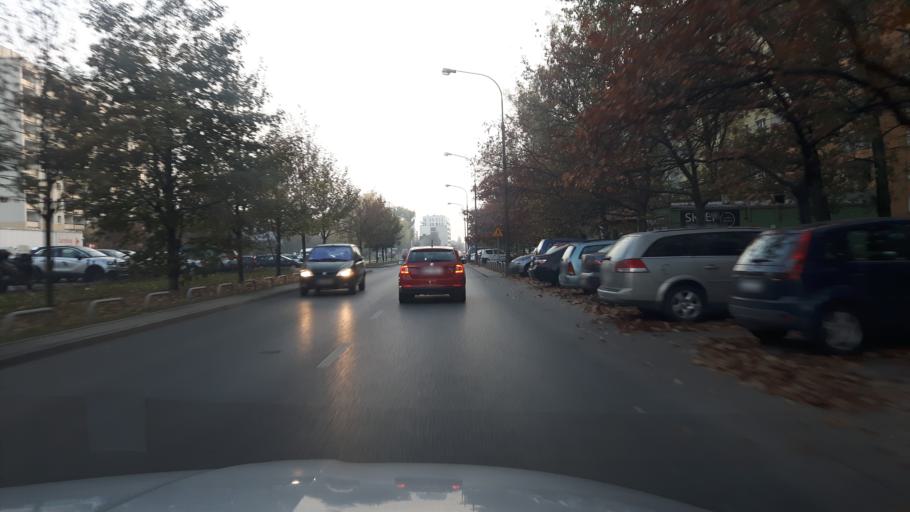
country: PL
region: Masovian Voivodeship
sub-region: Warszawa
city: Mokotow
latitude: 52.1765
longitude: 21.0133
